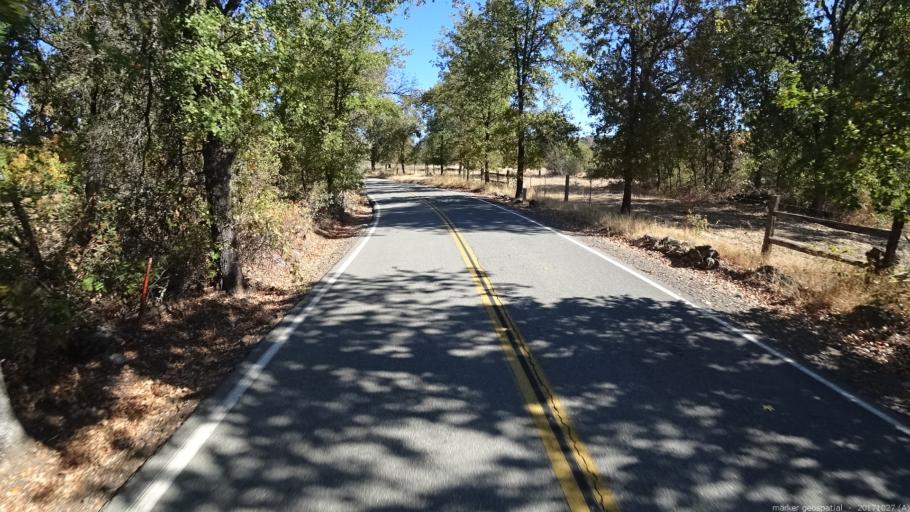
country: US
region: California
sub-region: Shasta County
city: Bella Vista
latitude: 40.7404
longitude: -121.9954
